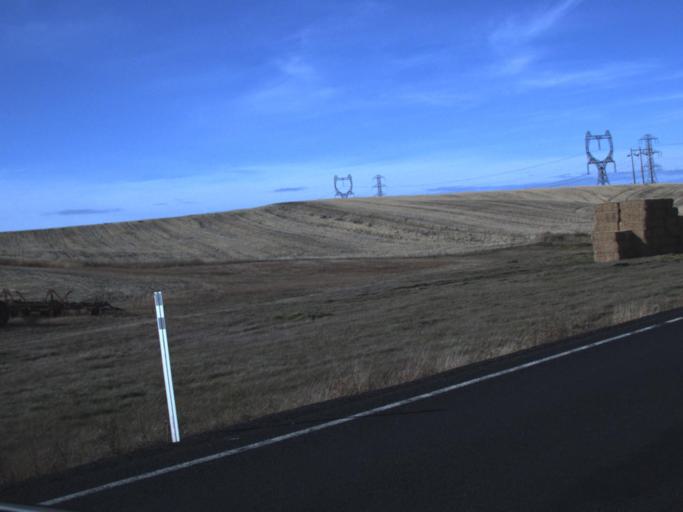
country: US
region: Washington
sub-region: Lincoln County
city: Davenport
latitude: 47.7299
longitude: -118.1610
